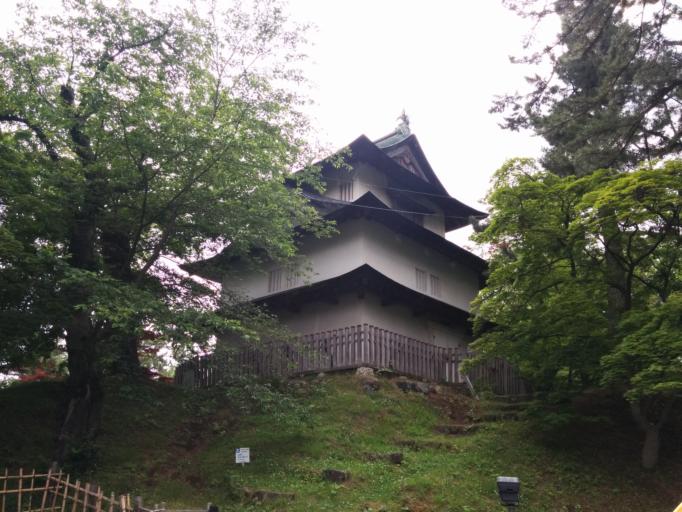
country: JP
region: Aomori
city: Hirosaki
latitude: 40.6090
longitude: 140.4660
